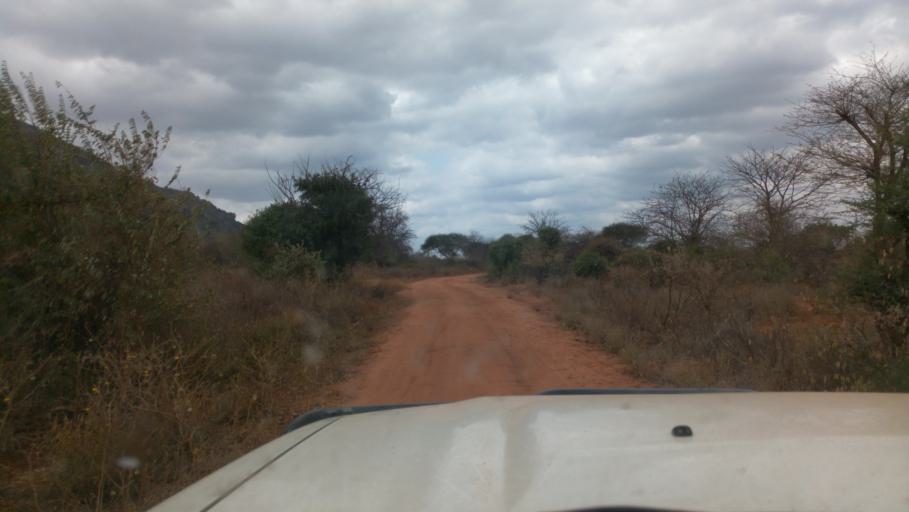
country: KE
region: Kitui
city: Kitui
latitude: -1.8858
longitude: 38.3960
